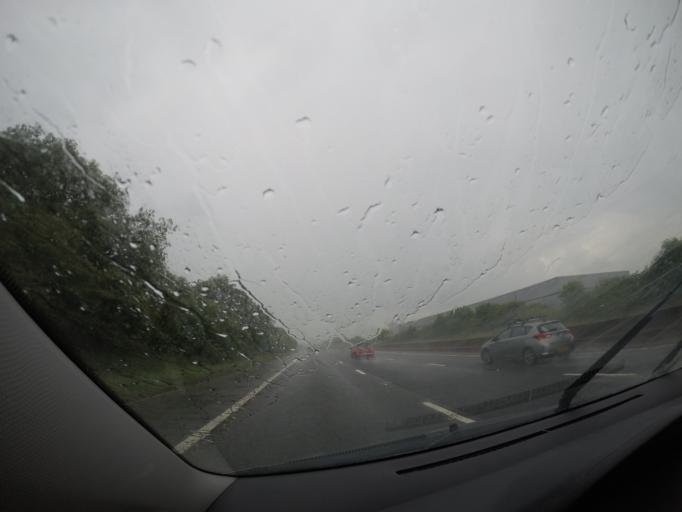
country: GB
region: England
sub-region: Cumbria
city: Penrith
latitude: 54.6645
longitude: -2.7730
